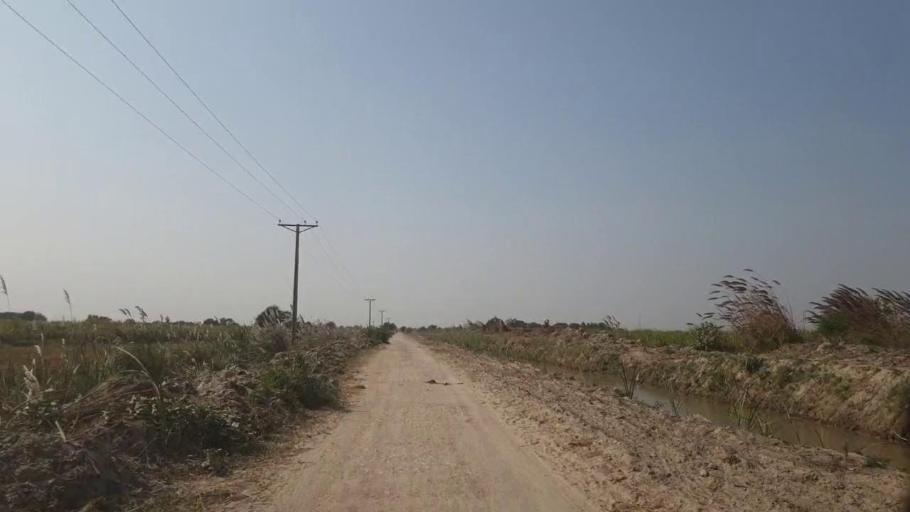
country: PK
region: Sindh
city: Bulri
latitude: 24.9516
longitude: 68.3742
